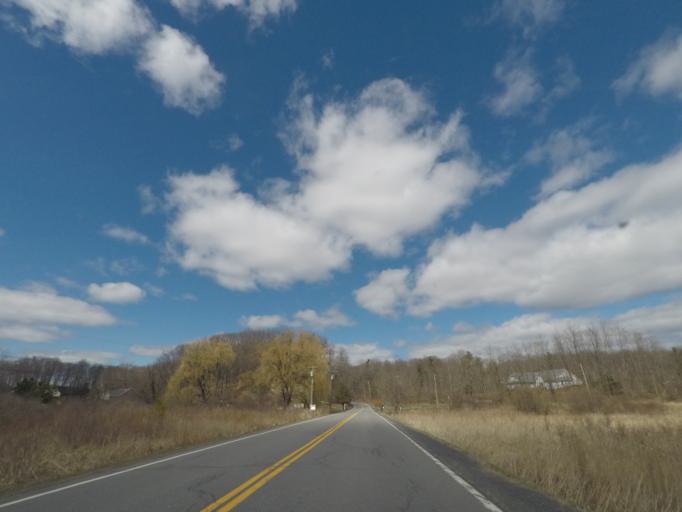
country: US
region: New York
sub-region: Albany County
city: Voorheesville
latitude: 42.6541
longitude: -73.9876
